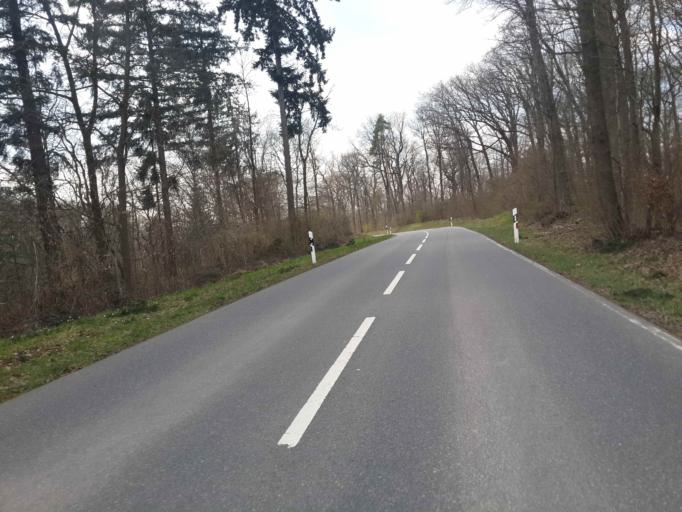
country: DE
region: Baden-Wuerttemberg
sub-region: Karlsruhe Region
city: Sinsheim
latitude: 49.2092
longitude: 8.8384
